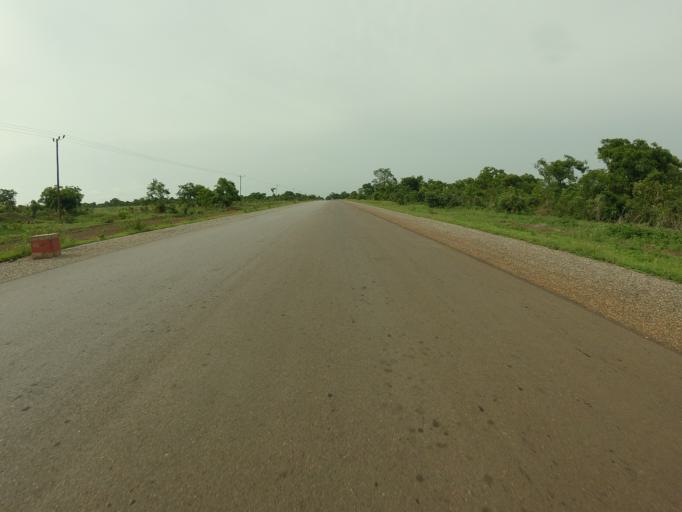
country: GH
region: Northern
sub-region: Yendi
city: Yendi
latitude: 9.6460
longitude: -0.0680
